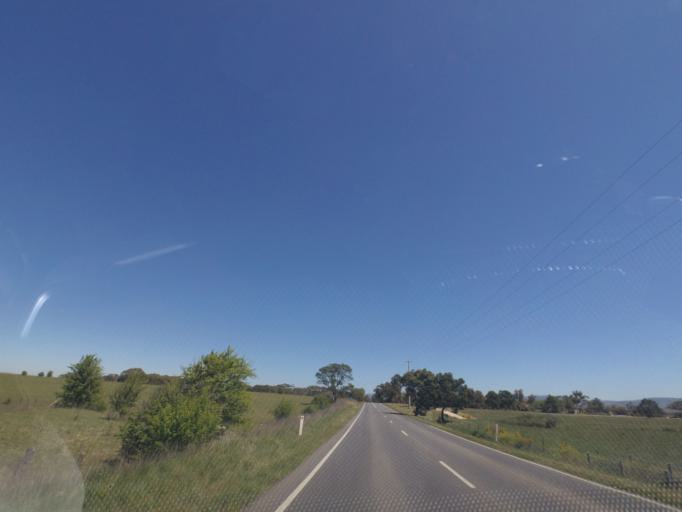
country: AU
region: Victoria
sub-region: Whittlesea
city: Whittlesea
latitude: -37.2946
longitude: 144.9379
